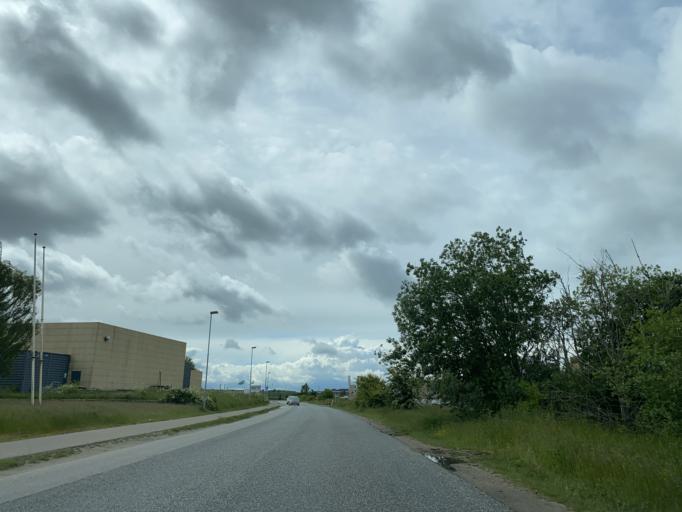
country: DK
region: Central Jutland
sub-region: Arhus Kommune
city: Stavtrup
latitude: 56.1869
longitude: 10.1292
